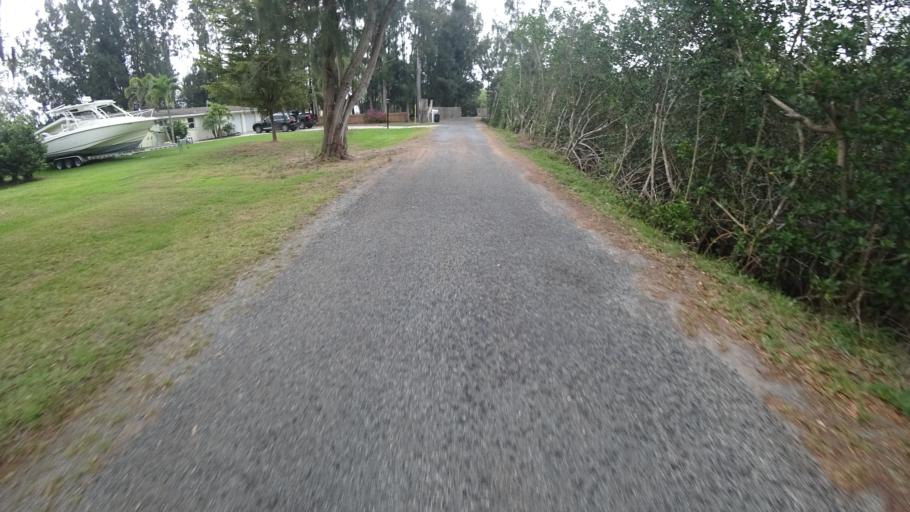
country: US
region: Florida
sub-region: Manatee County
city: Samoset
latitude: 27.4815
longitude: -82.5051
